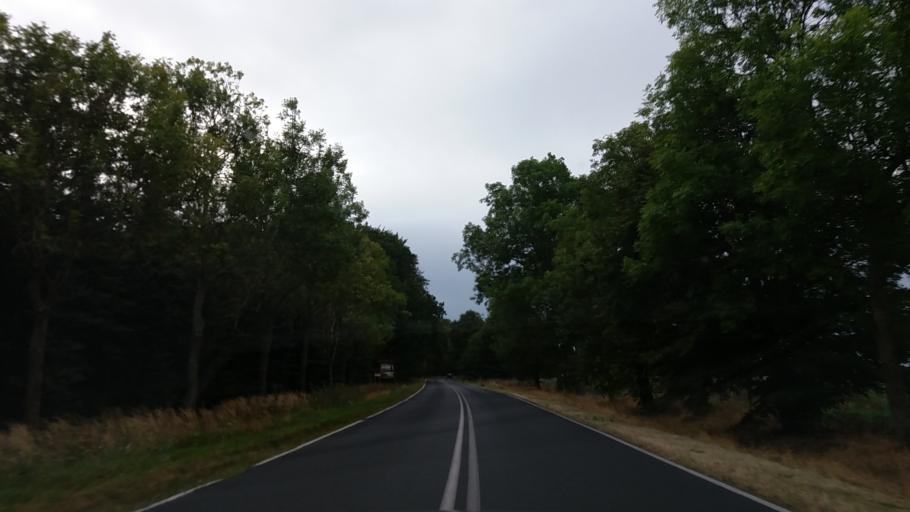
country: PL
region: West Pomeranian Voivodeship
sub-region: Powiat mysliborski
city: Barlinek
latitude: 52.9567
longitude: 15.1825
